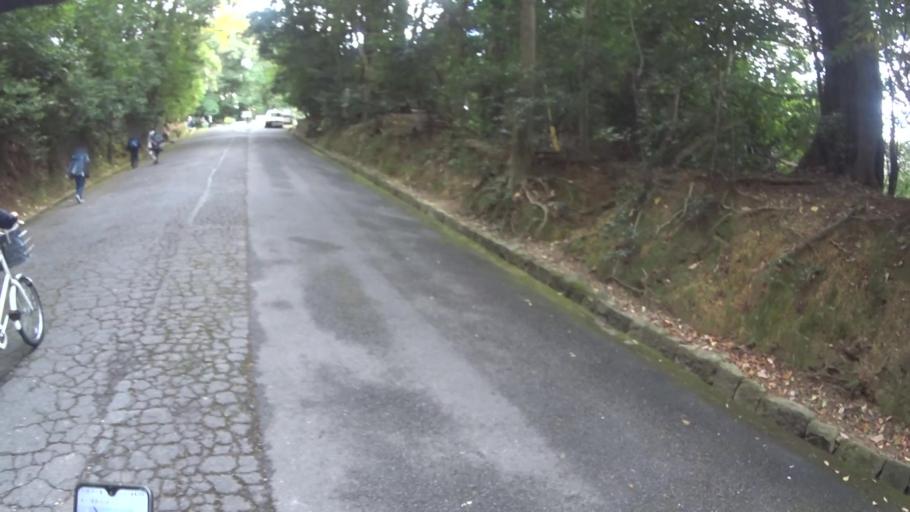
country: JP
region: Kyoto
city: Kyoto
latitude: 34.9789
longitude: 135.7795
